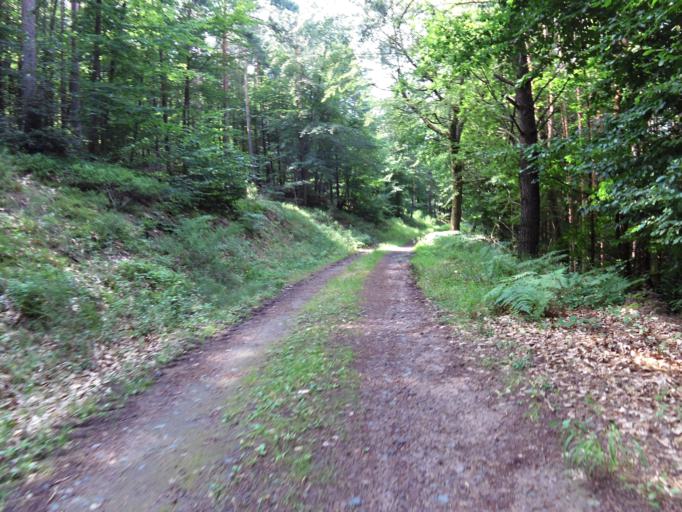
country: DE
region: Rheinland-Pfalz
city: Lindenberg
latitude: 49.4316
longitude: 8.0824
